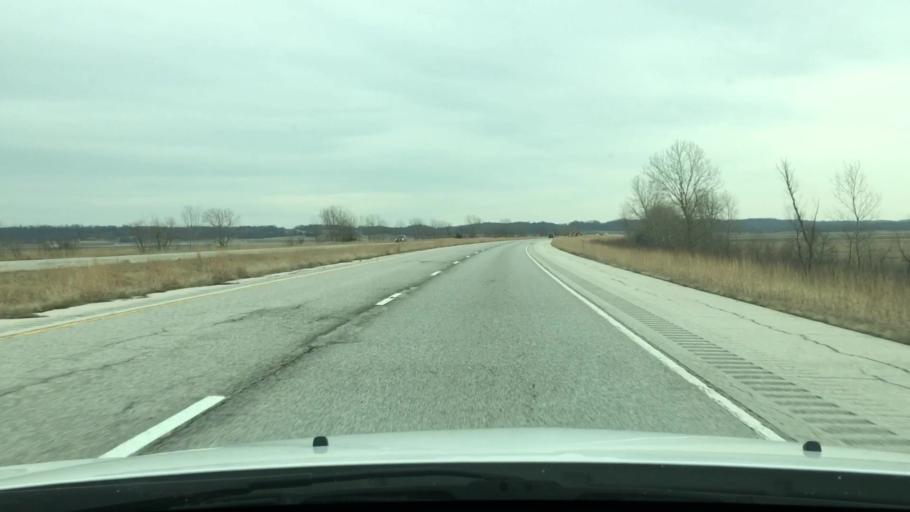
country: US
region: Illinois
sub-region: Pike County
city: Griggsville
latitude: 39.6912
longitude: -90.6073
